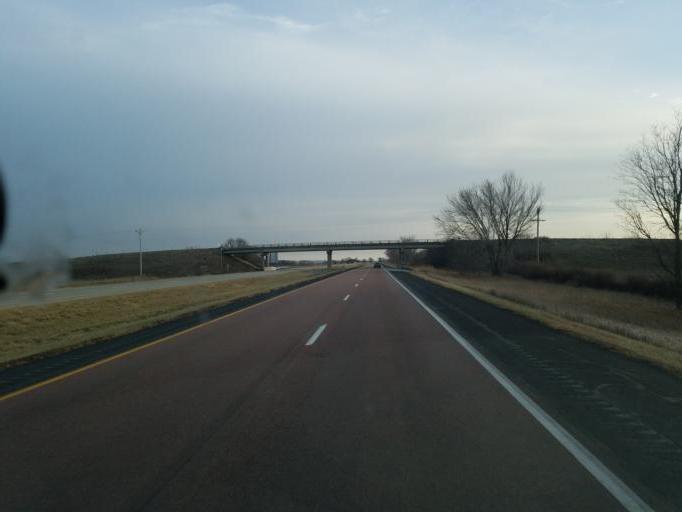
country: US
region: Iowa
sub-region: Monona County
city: Onawa
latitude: 41.9808
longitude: -96.1052
